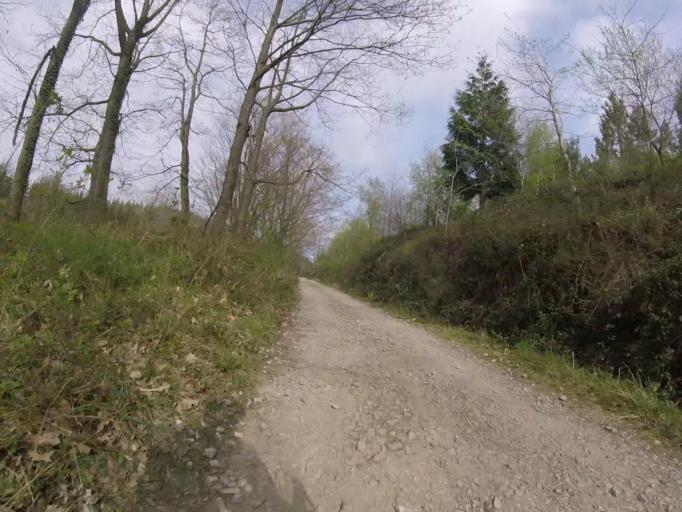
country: ES
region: Basque Country
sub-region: Provincia de Guipuzcoa
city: Usurbil
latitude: 43.2471
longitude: -2.0839
